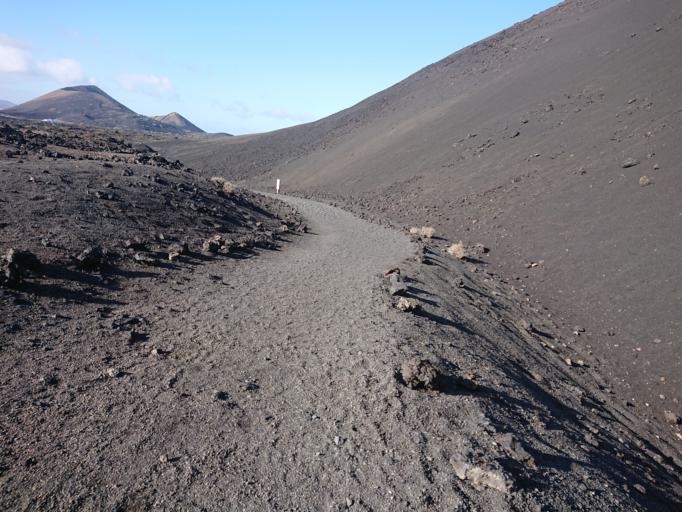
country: ES
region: Canary Islands
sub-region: Provincia de Las Palmas
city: Tias
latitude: 28.9903
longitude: -13.6917
